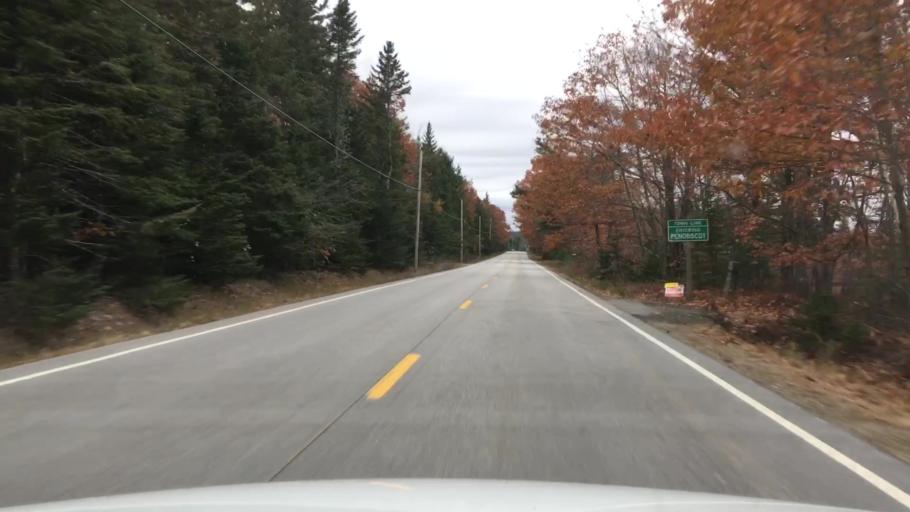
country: US
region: Maine
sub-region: Hancock County
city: Penobscot
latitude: 44.4877
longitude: -68.6421
